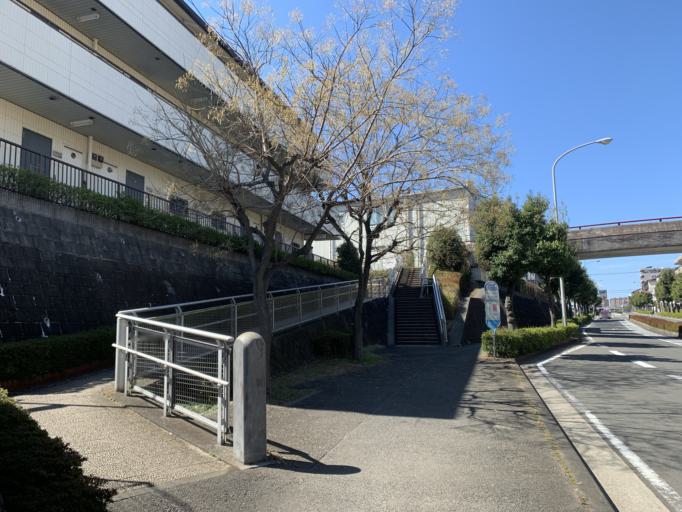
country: JP
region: Tokyo
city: Chofugaoka
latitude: 35.5540
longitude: 139.5851
